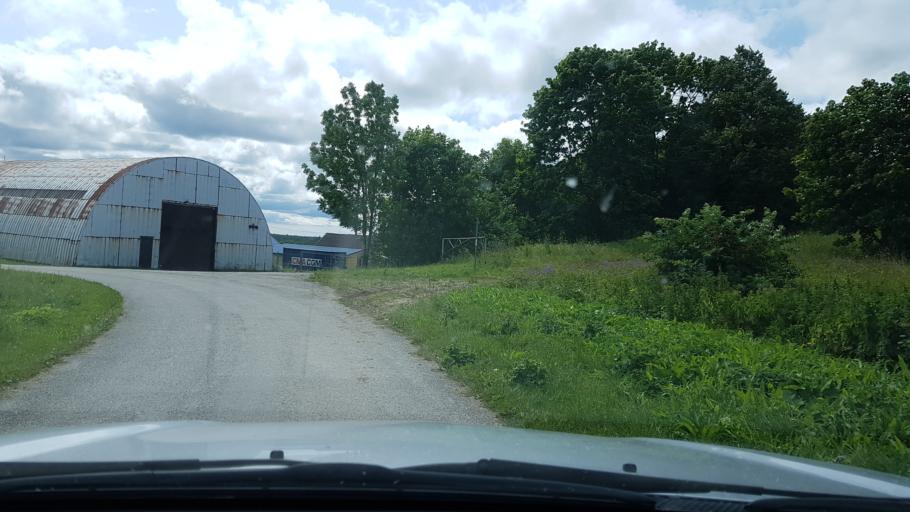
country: EE
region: Ida-Virumaa
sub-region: Sillamaee linn
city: Sillamae
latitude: 59.3743
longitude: 27.8680
